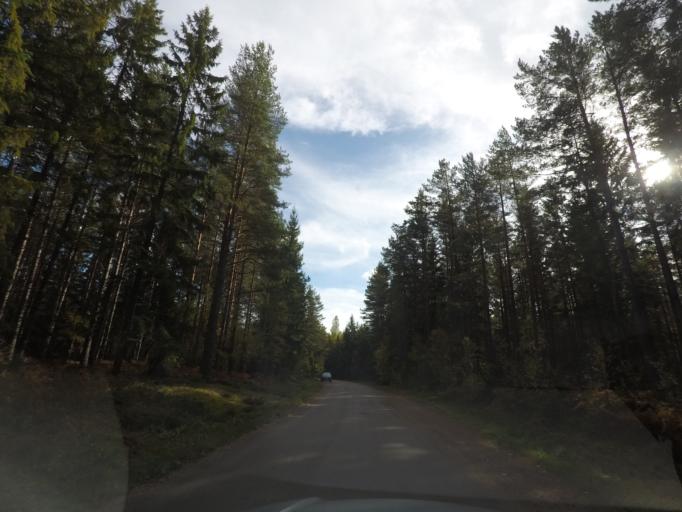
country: SE
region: Vaestmanland
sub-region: Kungsors Kommun
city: Kungsoer
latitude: 59.3357
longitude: 16.2150
